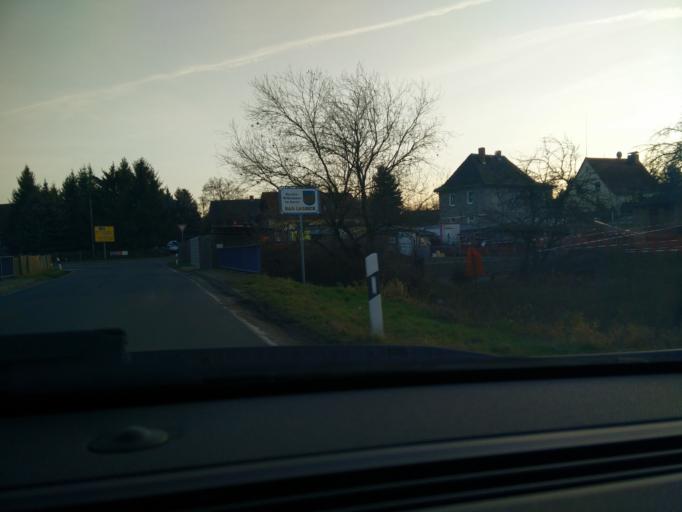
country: DE
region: Saxony
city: Bad Lausick
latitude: 51.1432
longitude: 12.6190
